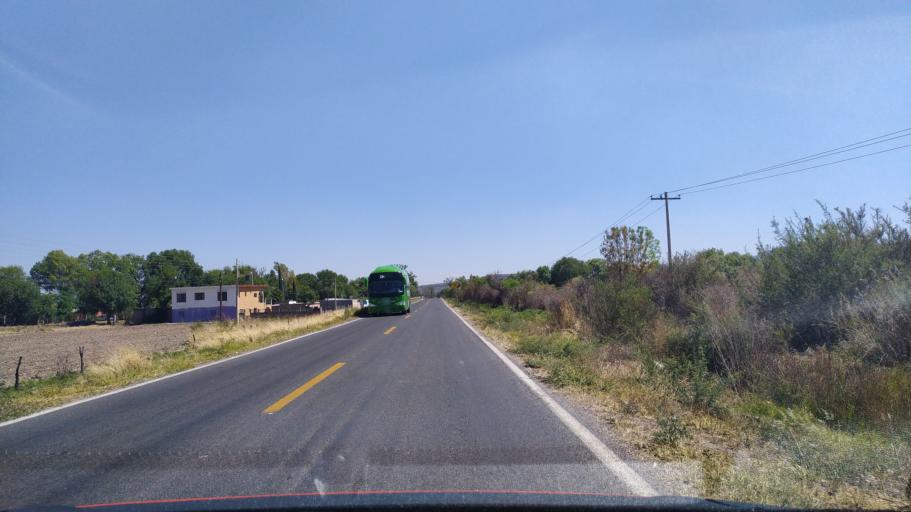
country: MX
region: Guanajuato
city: Ciudad Manuel Doblado
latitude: 20.7927
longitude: -101.9838
